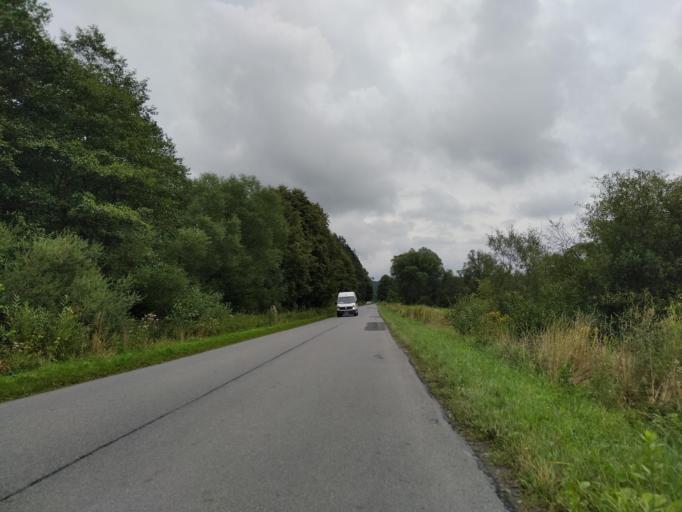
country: PL
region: Subcarpathian Voivodeship
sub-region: Powiat przemyski
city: Bircza
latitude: 49.6848
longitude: 22.4017
